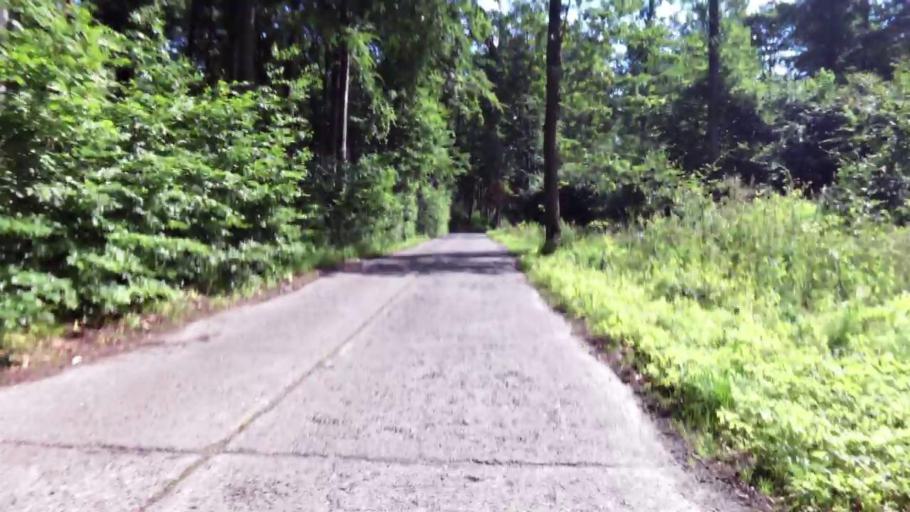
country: PL
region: West Pomeranian Voivodeship
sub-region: Powiat stargardzki
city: Dobrzany
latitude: 53.3896
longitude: 15.4678
